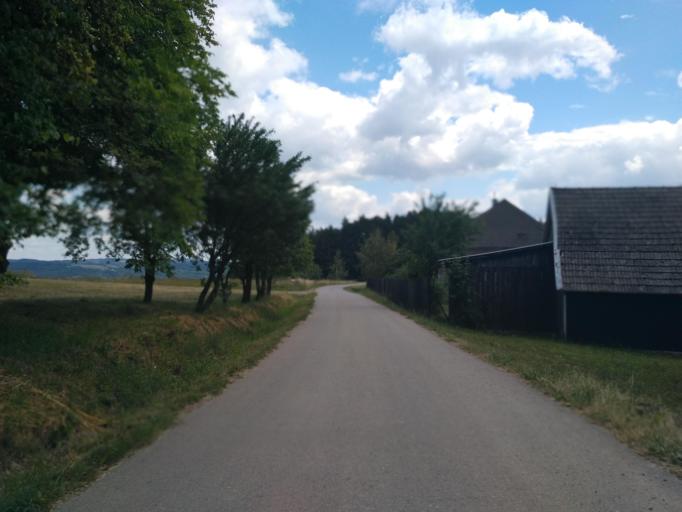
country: PL
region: Subcarpathian Voivodeship
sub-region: Powiat jasielski
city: Brzyska
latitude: 49.8077
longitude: 21.3768
